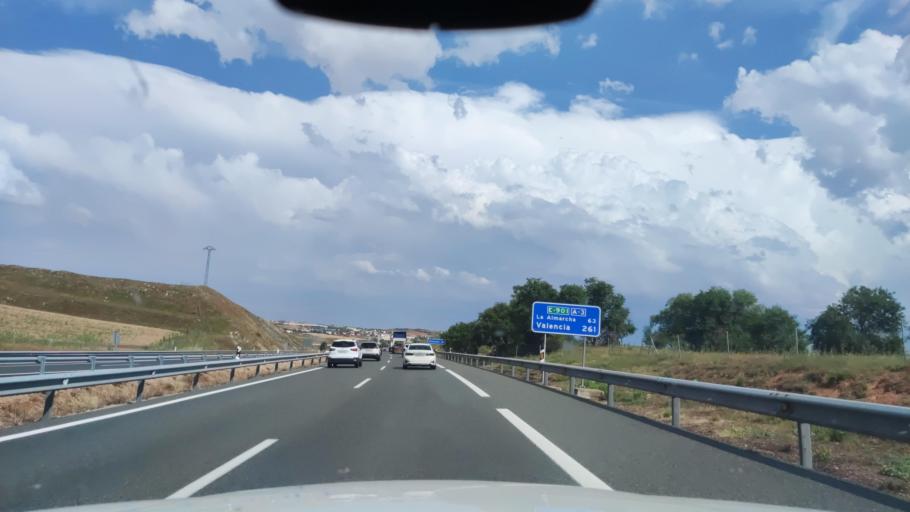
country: ES
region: Castille-La Mancha
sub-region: Provincia de Cuenca
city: Tribaldos
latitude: 39.9573
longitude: -2.9227
